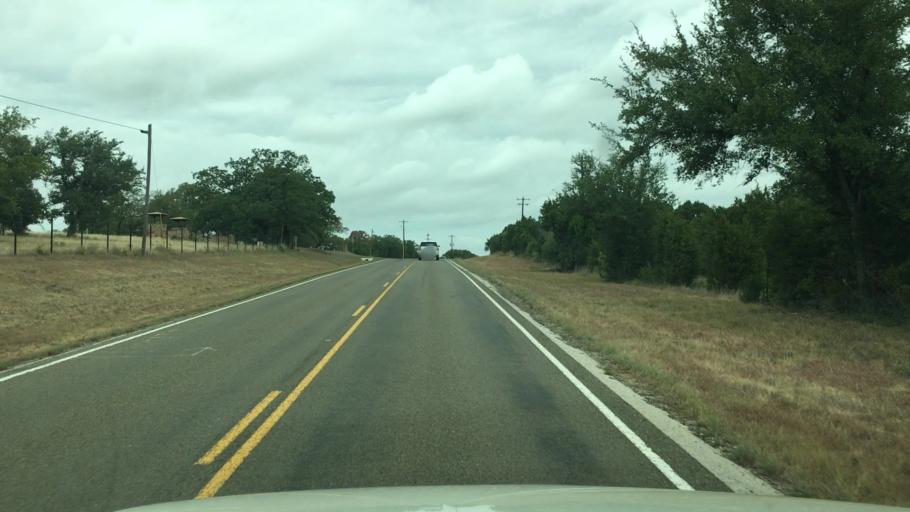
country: US
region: Texas
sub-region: Llano County
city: Horseshoe Bay
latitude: 30.4643
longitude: -98.4085
